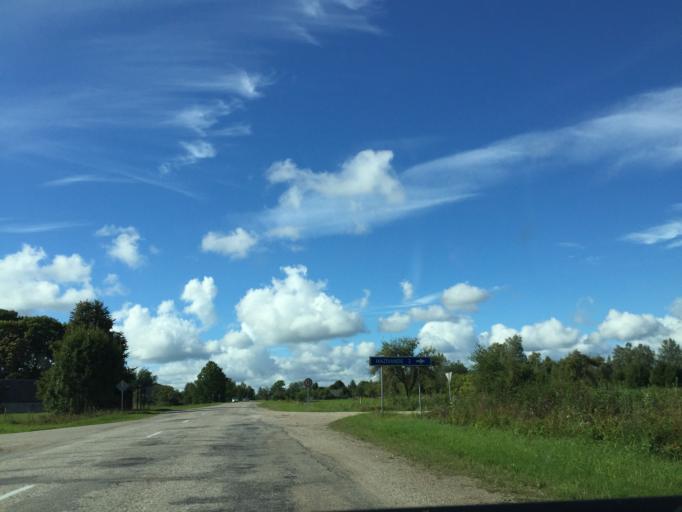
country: LV
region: Kuldigas Rajons
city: Kuldiga
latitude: 56.9914
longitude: 21.7686
